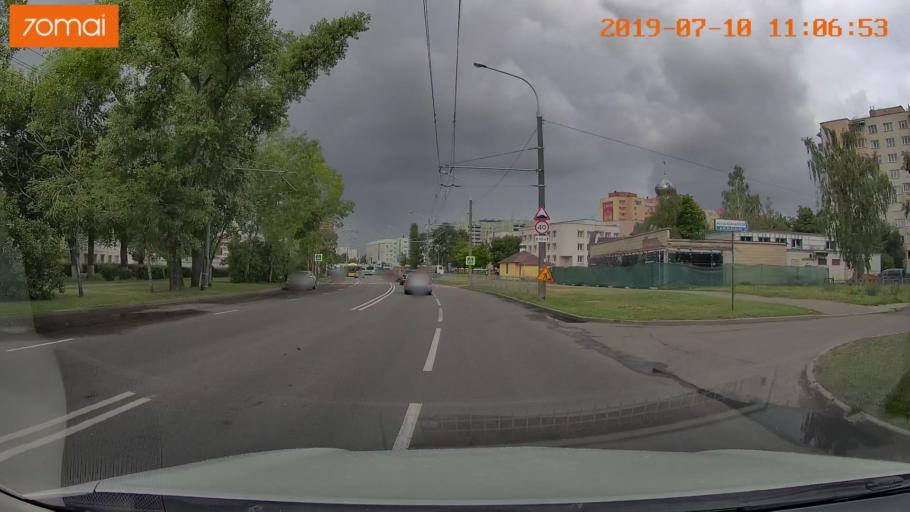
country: BY
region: Minsk
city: Syenitsa
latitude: 53.8493
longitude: 27.5408
